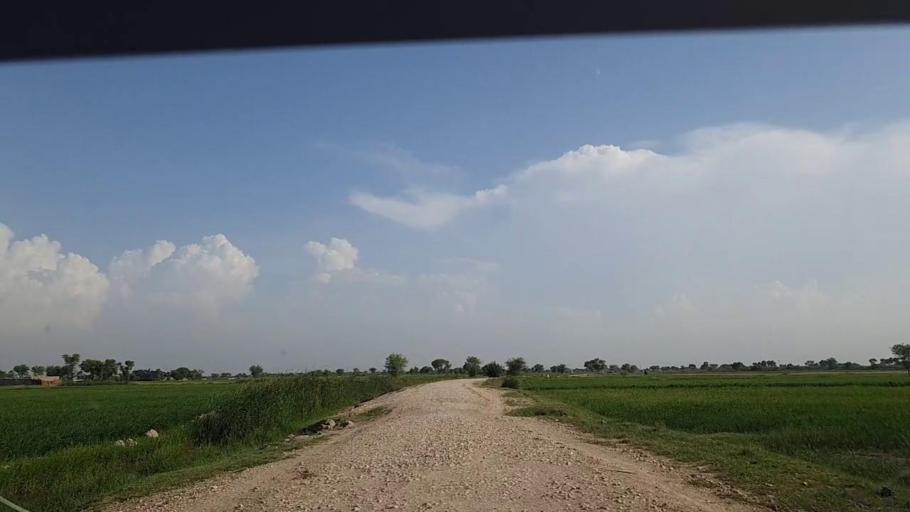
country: PK
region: Sindh
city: Khanpur
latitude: 27.8501
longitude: 69.3777
